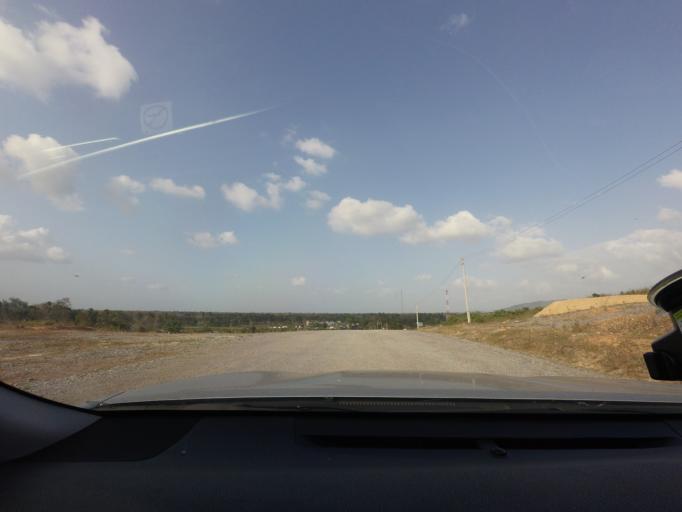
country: TH
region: Pattani
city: Mae Lan
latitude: 6.6120
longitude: 101.2560
